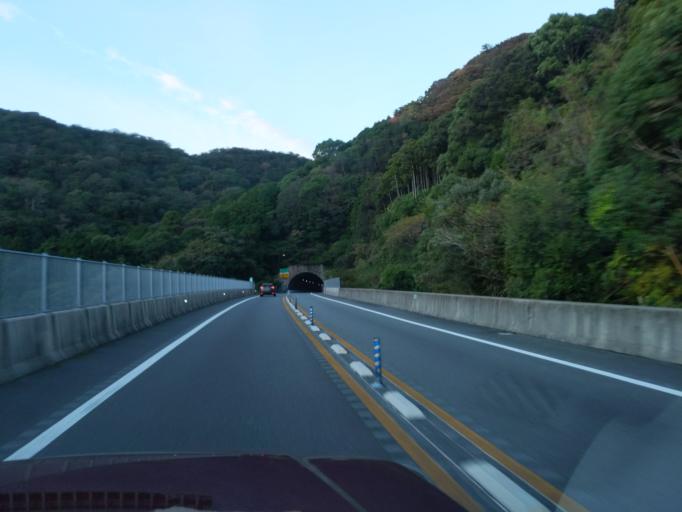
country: JP
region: Tokushima
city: Anan
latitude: 33.7585
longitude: 134.5608
